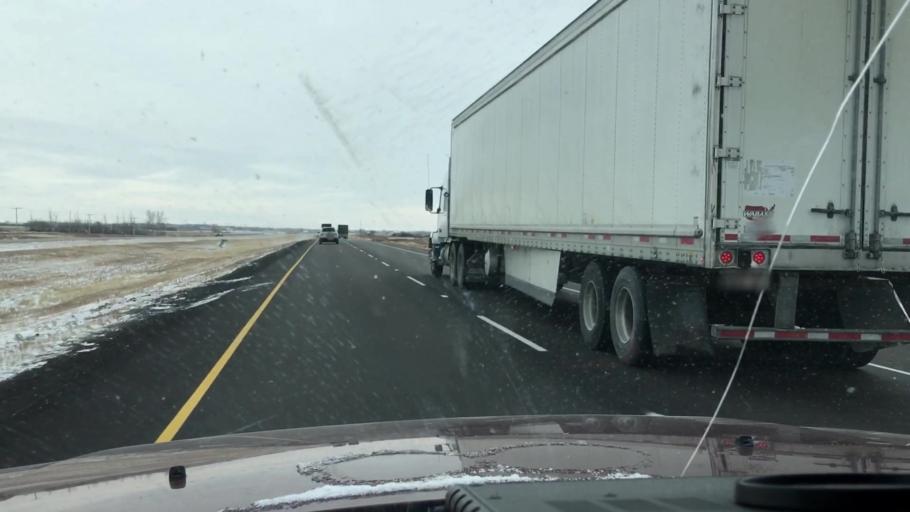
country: CA
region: Saskatchewan
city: Saskatoon
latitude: 51.7899
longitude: -106.4830
